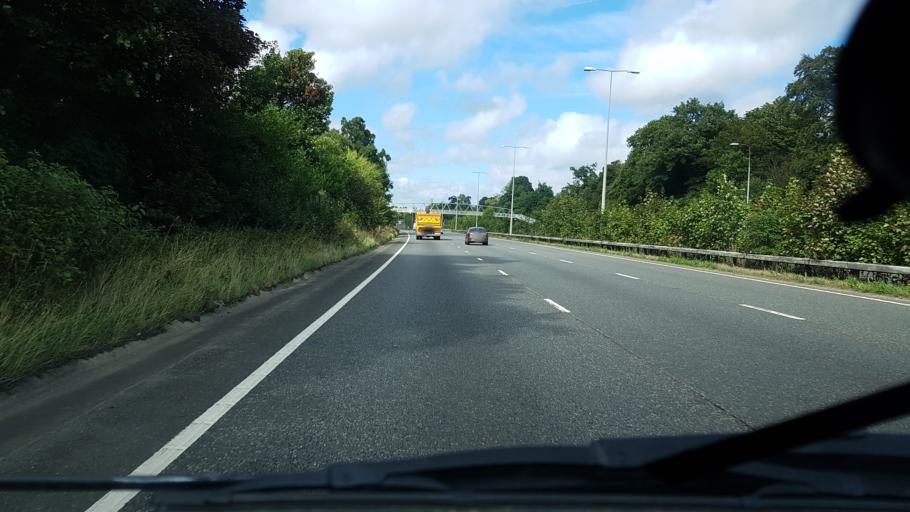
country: GB
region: England
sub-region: West Sussex
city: Broadfield
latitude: 51.0727
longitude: -0.2041
